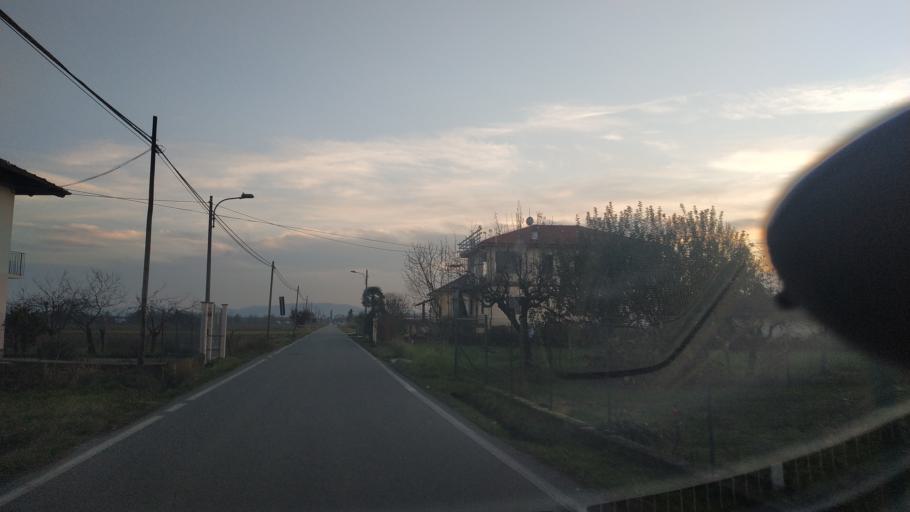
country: IT
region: Piedmont
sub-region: Provincia di Torino
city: Caluso
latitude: 45.2780
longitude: 7.8778
